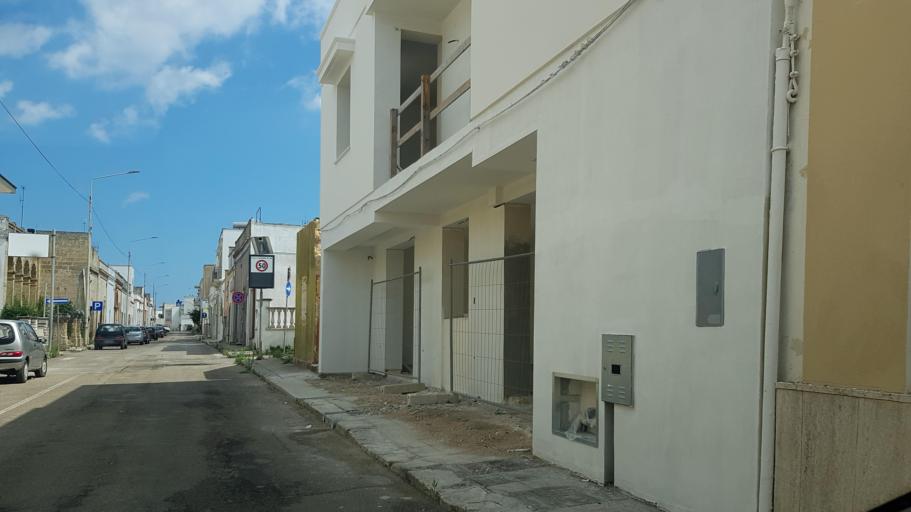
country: IT
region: Apulia
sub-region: Provincia di Lecce
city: Castrignano del Capo
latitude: 39.8369
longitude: 18.3469
